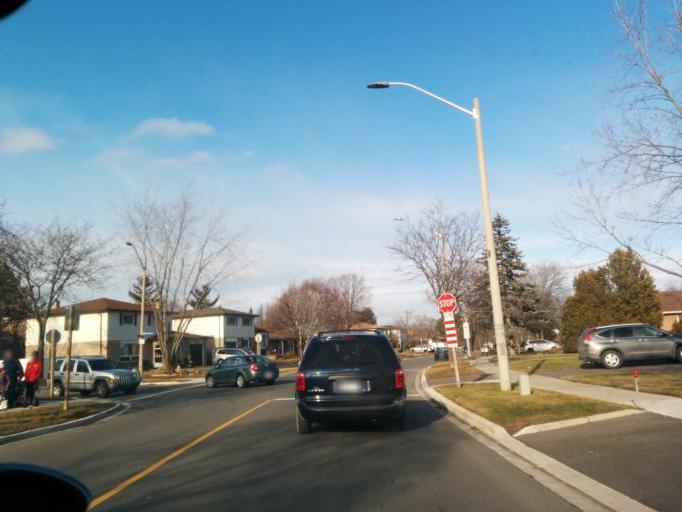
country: CA
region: Ontario
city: Mississauga
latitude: 43.5250
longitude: -79.6743
